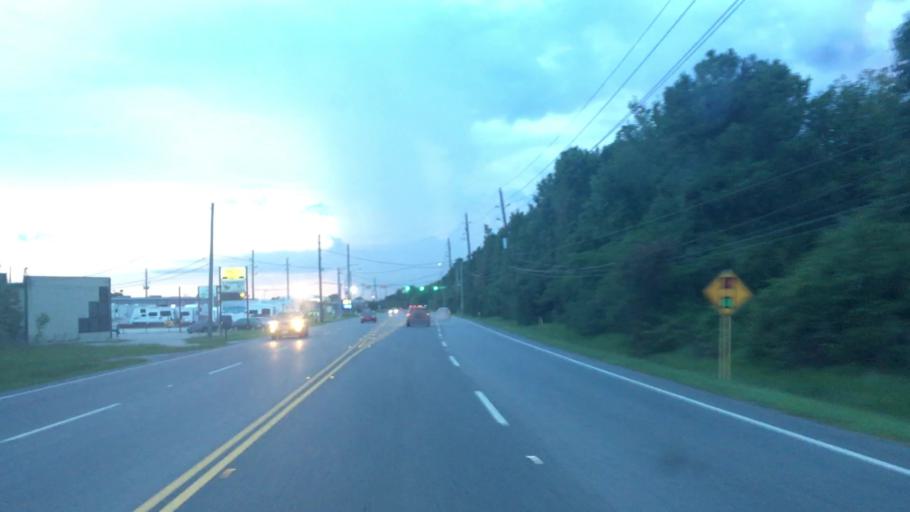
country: US
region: Texas
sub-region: Harris County
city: Humble
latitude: 29.9752
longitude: -95.2250
